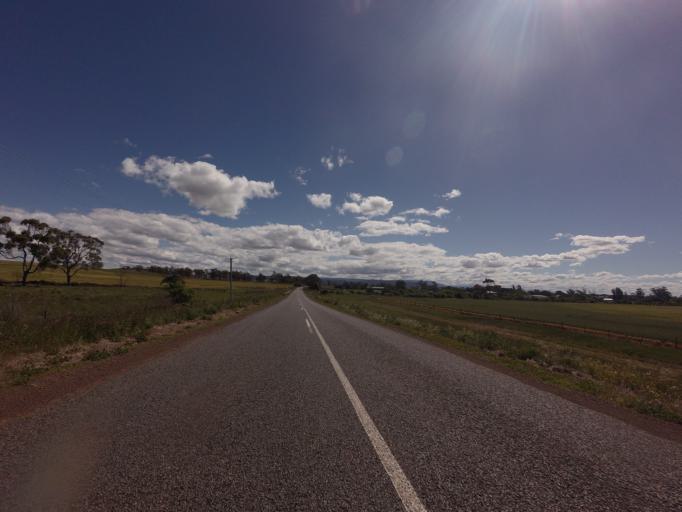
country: AU
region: Tasmania
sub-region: Northern Midlands
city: Evandale
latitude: -41.9411
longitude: 147.5414
